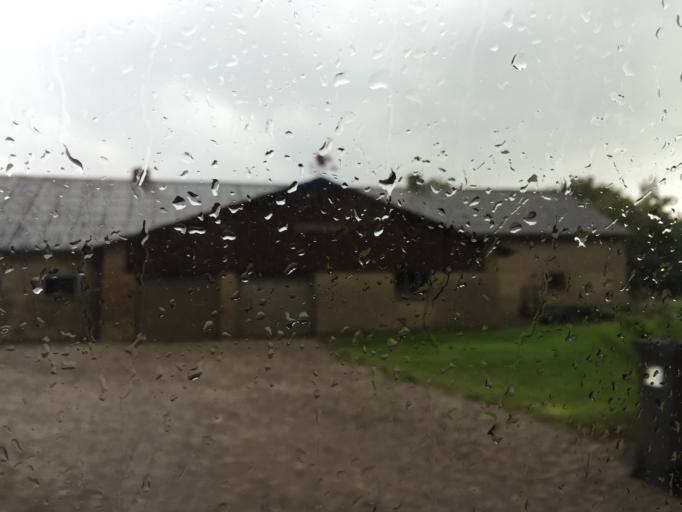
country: DK
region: South Denmark
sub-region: Sonderborg Kommune
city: Dybbol
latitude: 54.9551
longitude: 9.7403
